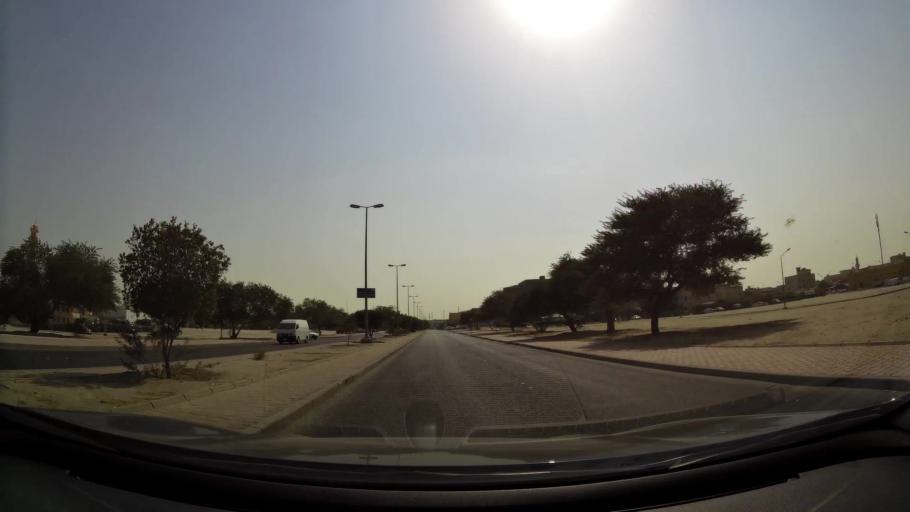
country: KW
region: Al Ahmadi
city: Al Fahahil
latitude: 29.0792
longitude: 48.1180
